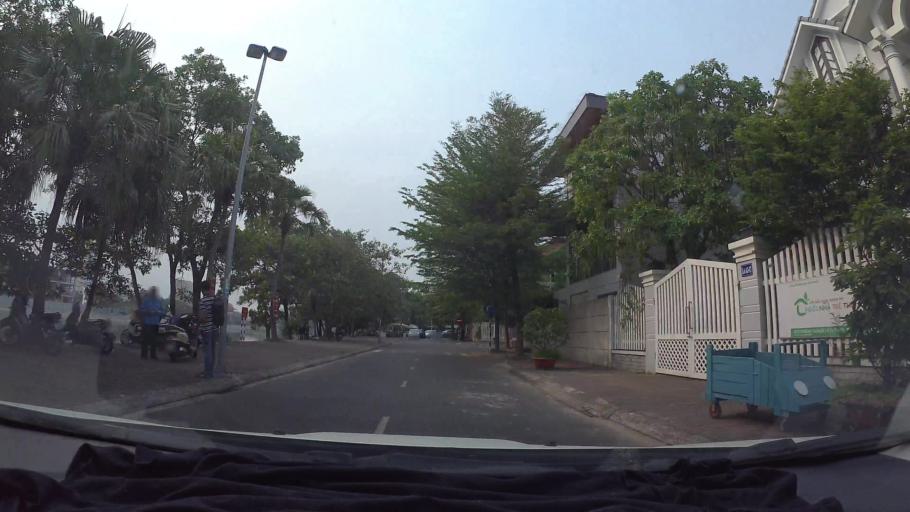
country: VN
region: Da Nang
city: Son Tra
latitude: 16.0469
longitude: 108.2261
